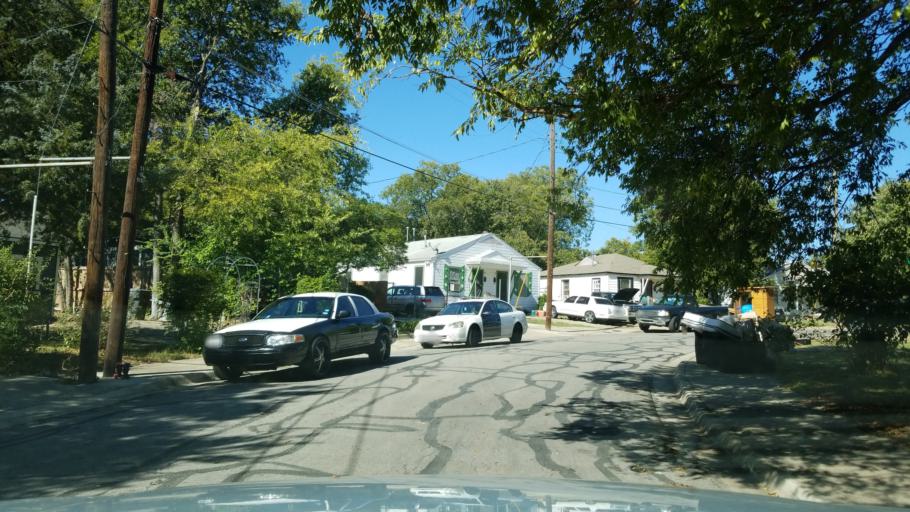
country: US
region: Texas
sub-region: Dallas County
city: Dallas
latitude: 32.7804
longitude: -96.7463
